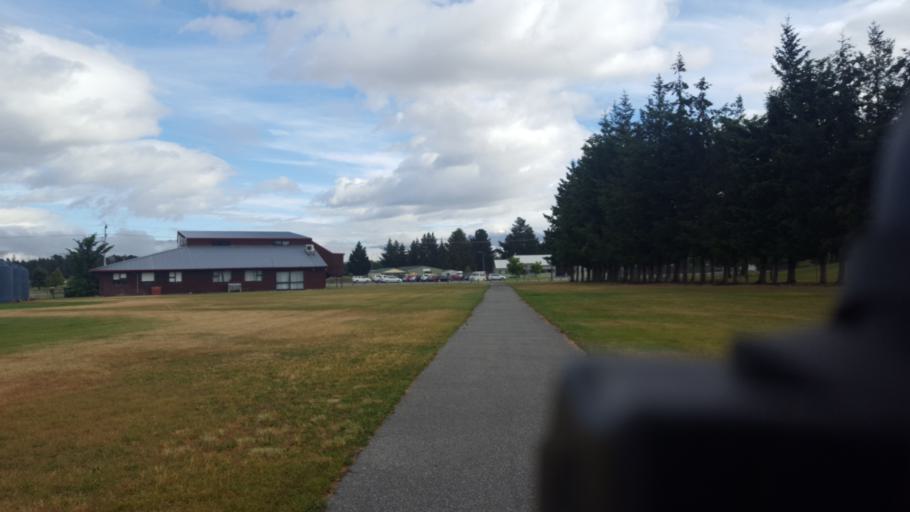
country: NZ
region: Otago
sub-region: Queenstown-Lakes District
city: Wanaka
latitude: -45.2441
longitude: 169.3820
